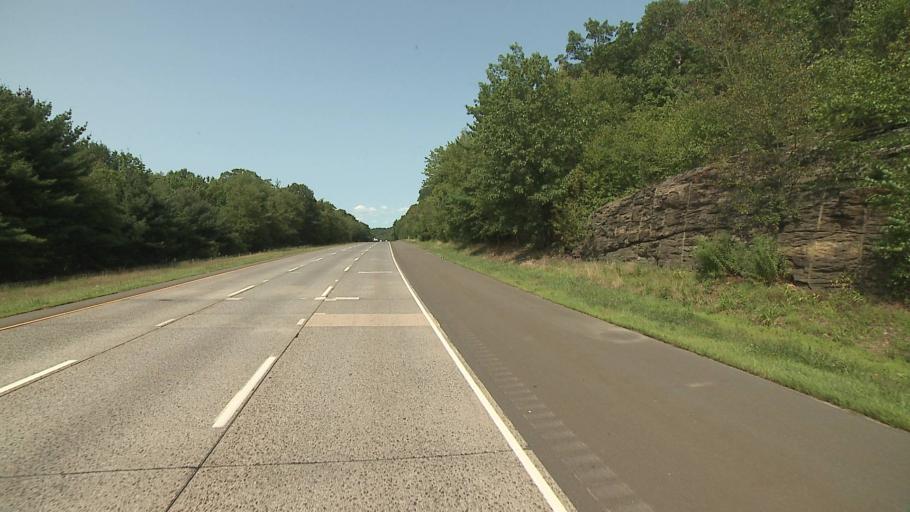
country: US
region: Connecticut
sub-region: Fairfield County
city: Trumbull
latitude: 41.2646
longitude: -73.2097
